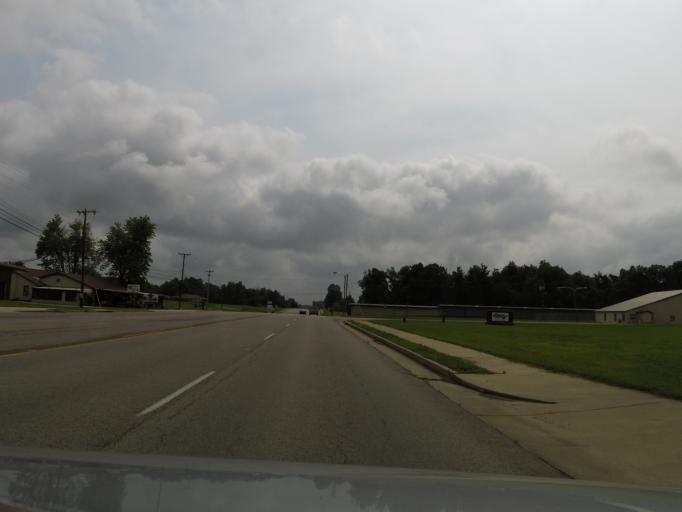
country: US
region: Kentucky
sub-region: Hopkins County
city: Madisonville
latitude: 37.3274
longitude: -87.4465
